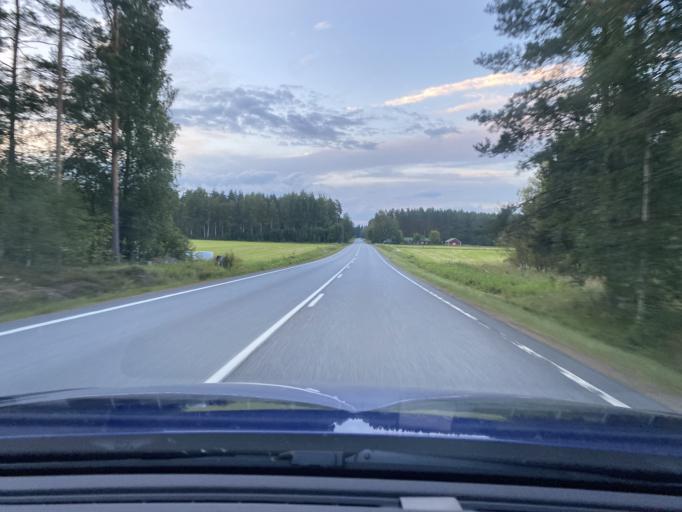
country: FI
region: Satakunta
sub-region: Pohjois-Satakunta
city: Honkajoki
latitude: 62.0441
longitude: 22.2431
